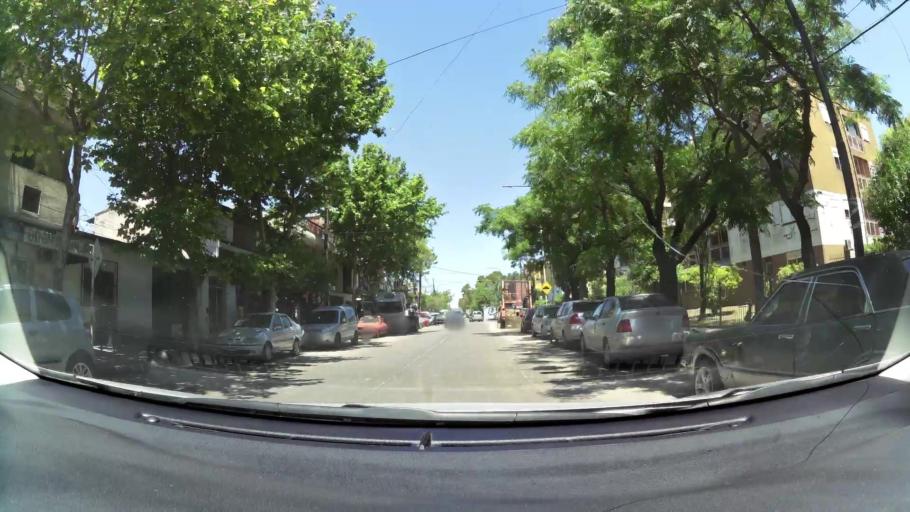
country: AR
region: Buenos Aires
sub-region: Partido de Avellaneda
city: Avellaneda
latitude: -34.6553
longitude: -58.4030
